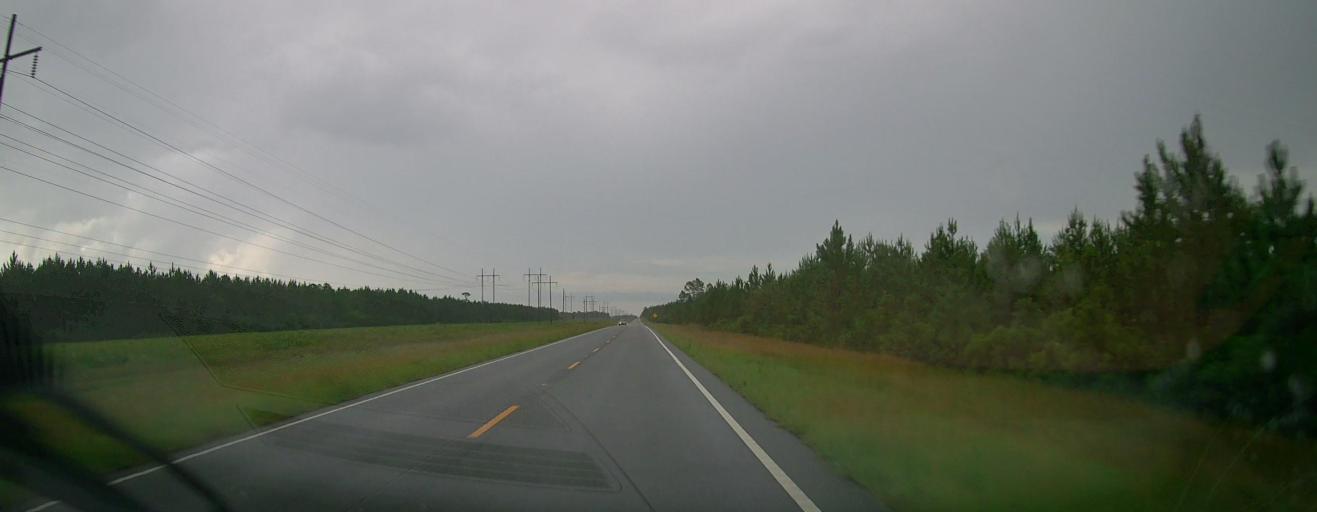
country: US
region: Georgia
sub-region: Brantley County
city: Nahunta
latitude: 31.3364
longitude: -81.8747
